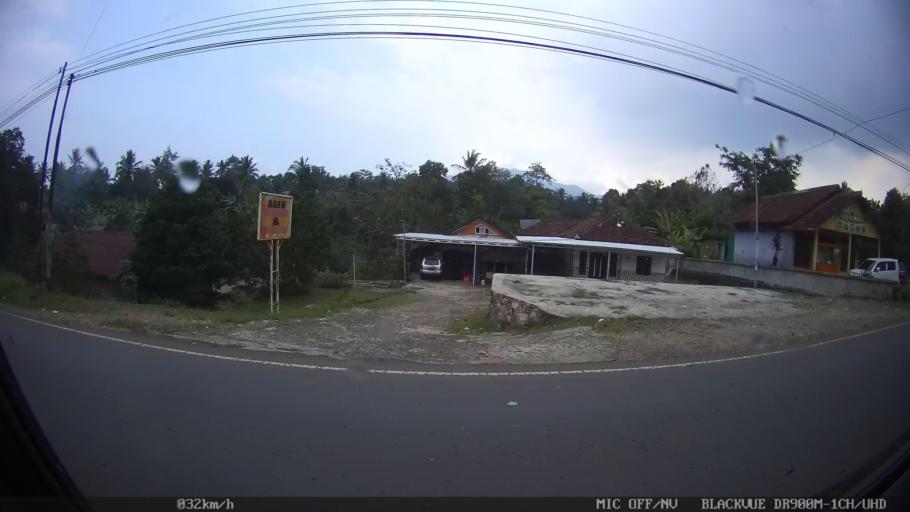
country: ID
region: Lampung
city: Gedongtataan
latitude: -5.3668
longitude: 105.1434
